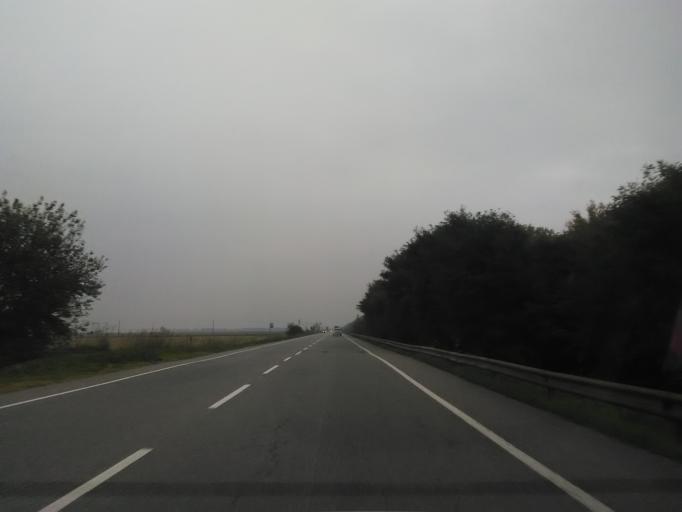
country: IT
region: Piedmont
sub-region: Provincia di Vercelli
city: Santhia
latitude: 45.3605
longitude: 8.1981
